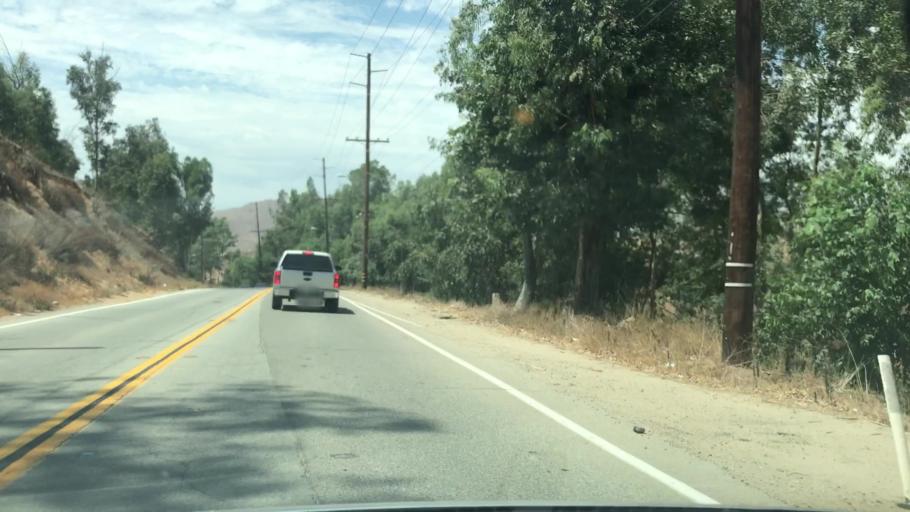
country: US
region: California
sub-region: Riverside County
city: Lake Elsinore
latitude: 33.7166
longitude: -117.3859
